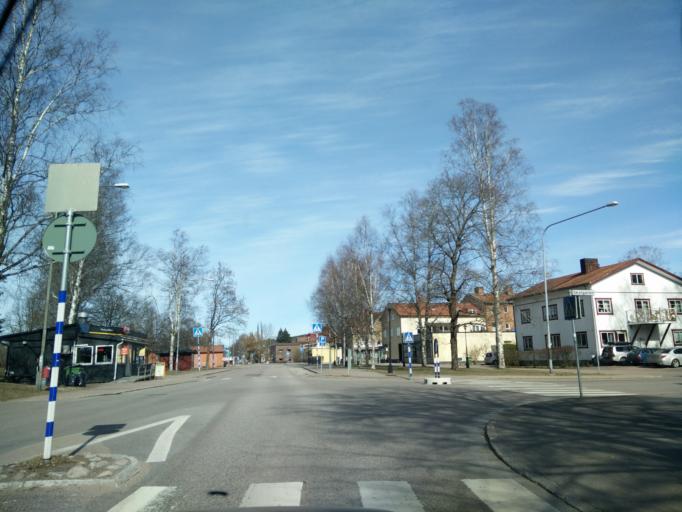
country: SE
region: Vaermland
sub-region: Hagfors Kommun
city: Hagfors
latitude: 60.0310
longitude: 13.6975
